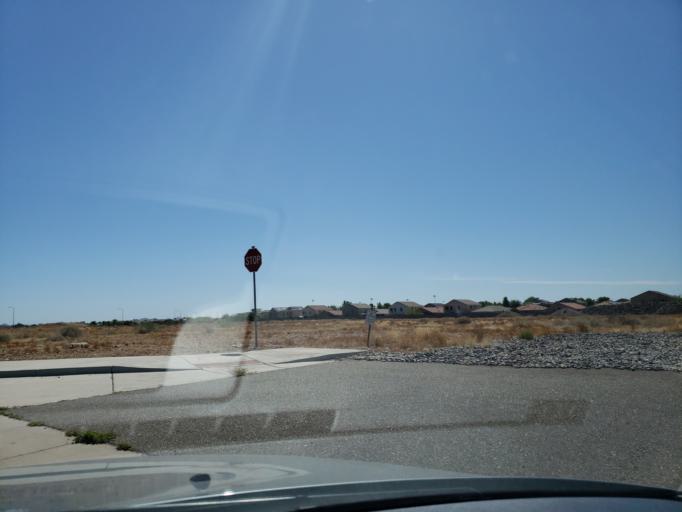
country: US
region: Arizona
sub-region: Maricopa County
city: Sun City West
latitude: 33.6816
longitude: -112.2730
